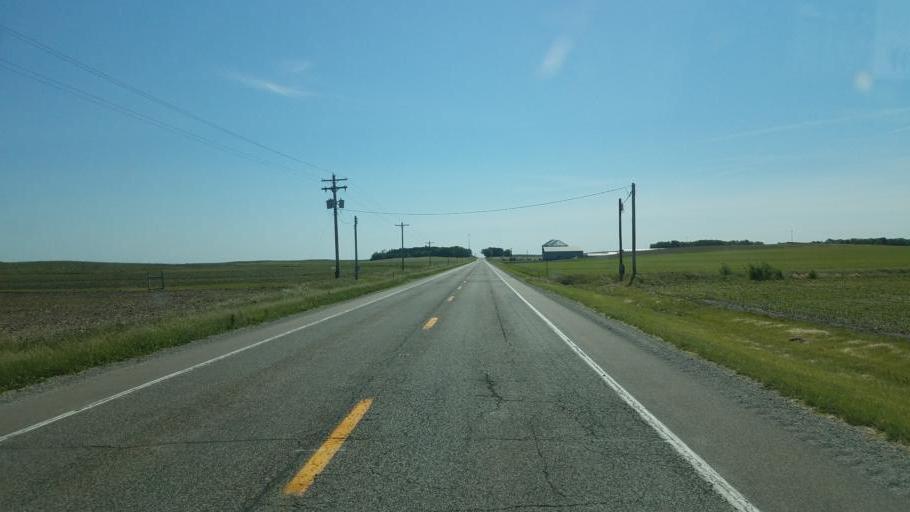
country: US
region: Illinois
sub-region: Mason County
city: Manito
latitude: 40.3033
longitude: -89.7965
